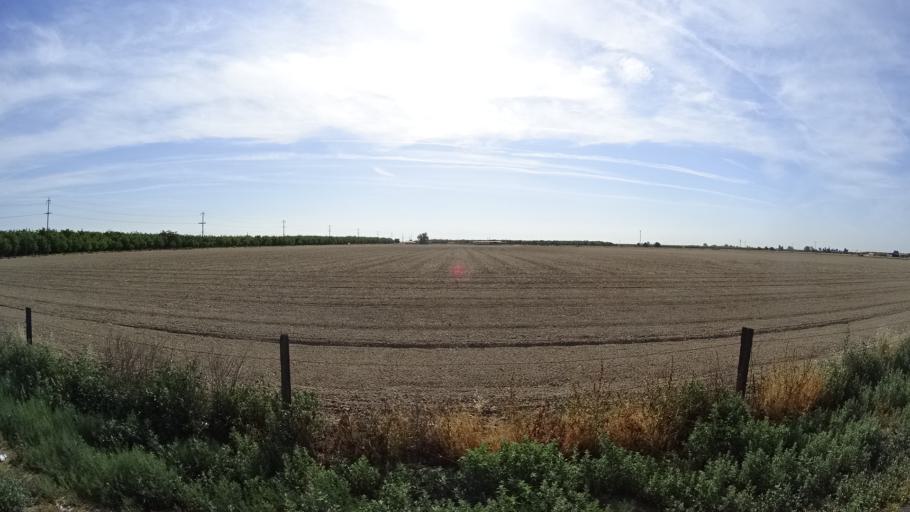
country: US
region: California
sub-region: Tulare County
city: Goshen
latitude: 36.3416
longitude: -119.4932
